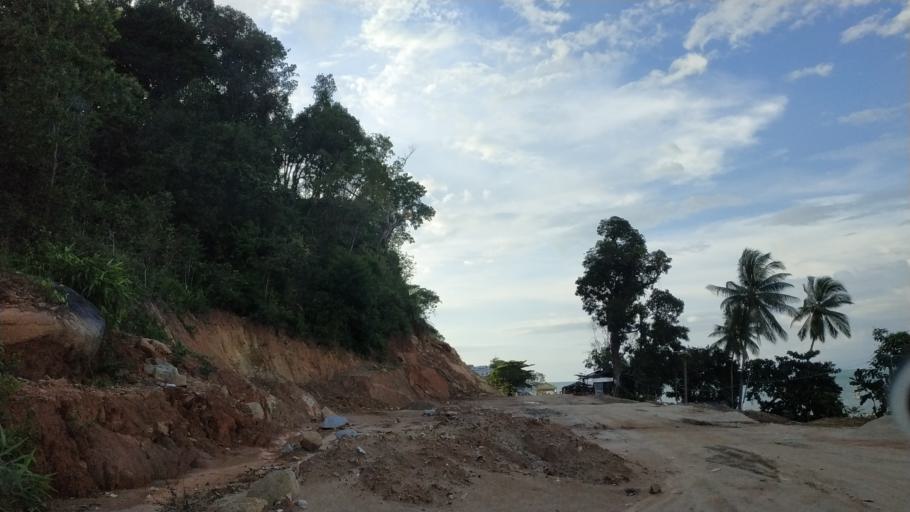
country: MM
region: Tanintharyi
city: Dawei
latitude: 14.0845
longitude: 98.0724
